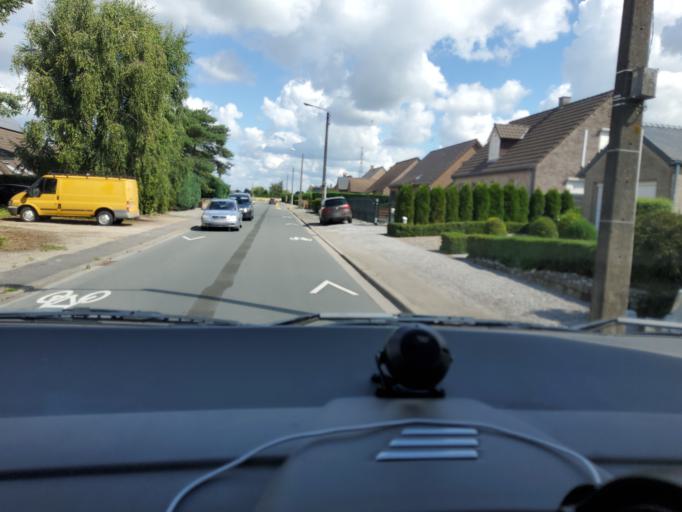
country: BE
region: Wallonia
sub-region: Province du Hainaut
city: Fleurus
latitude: 50.4899
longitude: 4.5503
